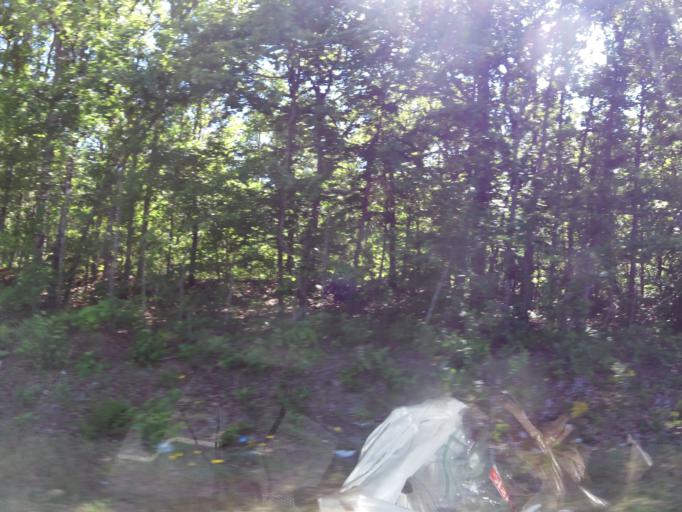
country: US
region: South Carolina
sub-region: Barnwell County
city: Williston
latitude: 33.5027
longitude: -81.5373
